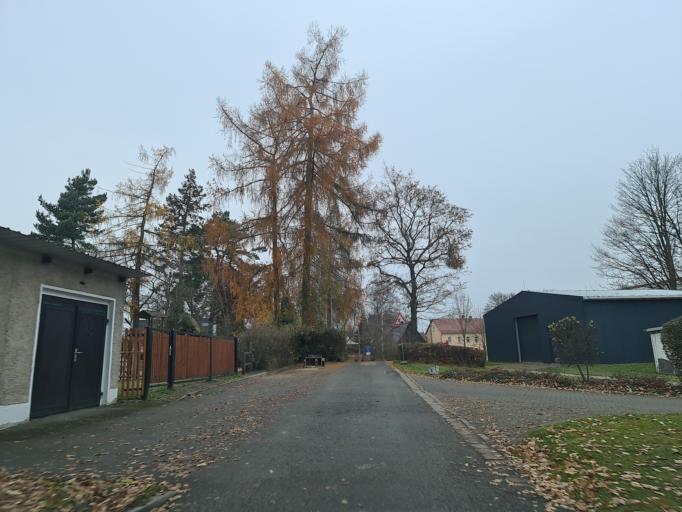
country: DE
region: Saxony
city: Syrau
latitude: 50.5211
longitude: 12.0925
